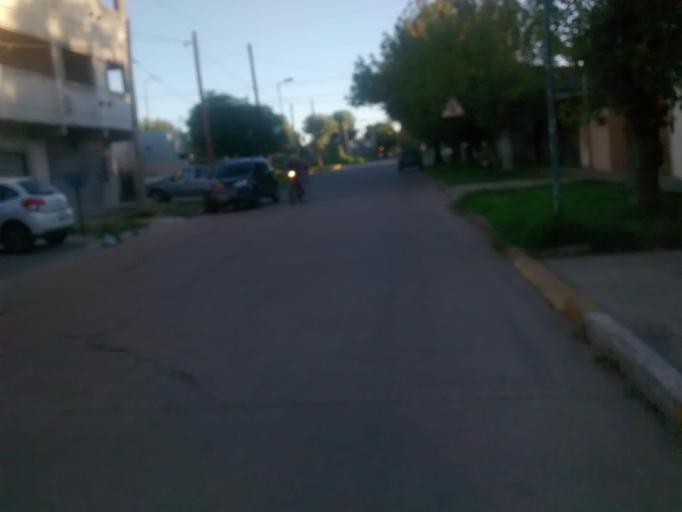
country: AR
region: Buenos Aires
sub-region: Partido de La Plata
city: La Plata
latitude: -34.9119
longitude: -57.9235
